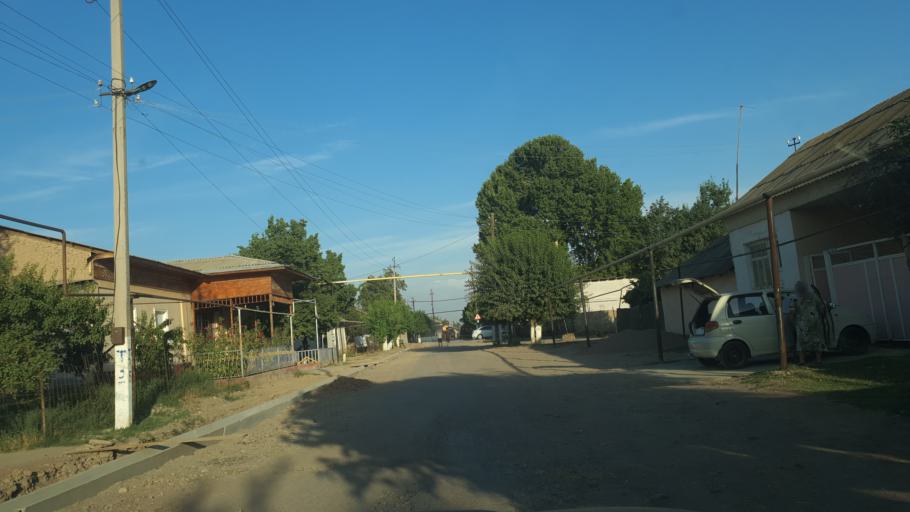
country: UZ
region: Toshkent
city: Tuytepa
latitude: 41.1036
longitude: 69.3998
